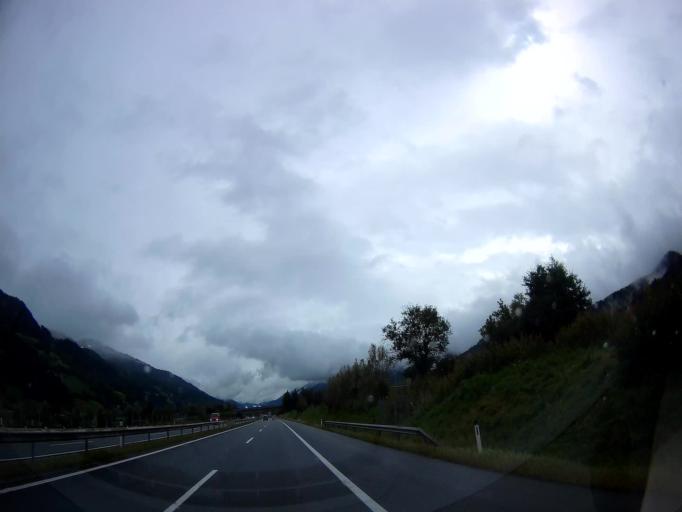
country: AT
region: Styria
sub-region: Politischer Bezirk Liezen
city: Trieben
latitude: 47.5108
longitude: 14.4245
